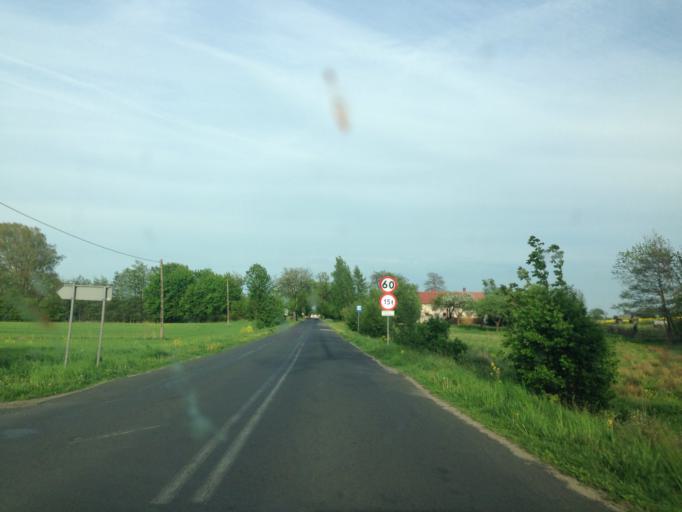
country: PL
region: Kujawsko-Pomorskie
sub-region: Powiat chelminski
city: Lisewo
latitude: 53.2925
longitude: 18.7301
